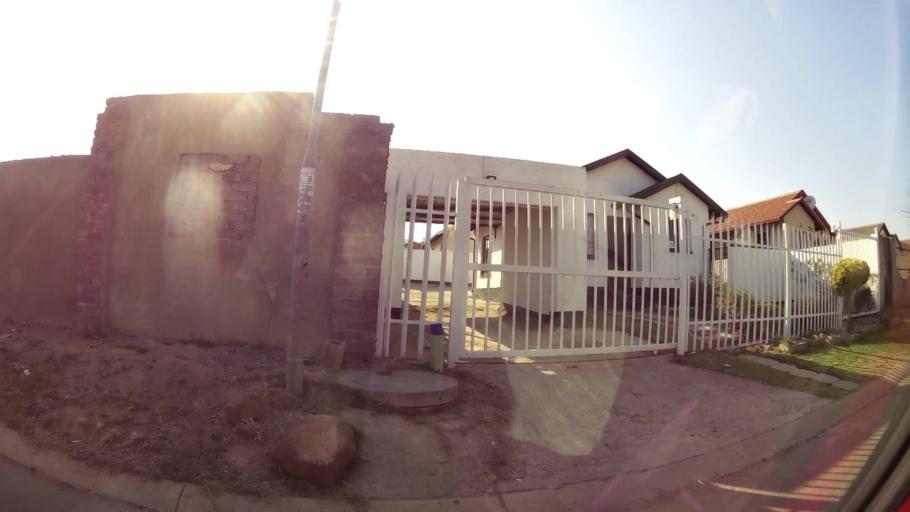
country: ZA
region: Gauteng
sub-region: City of Johannesburg Metropolitan Municipality
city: Soweto
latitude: -26.2874
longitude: 27.9512
